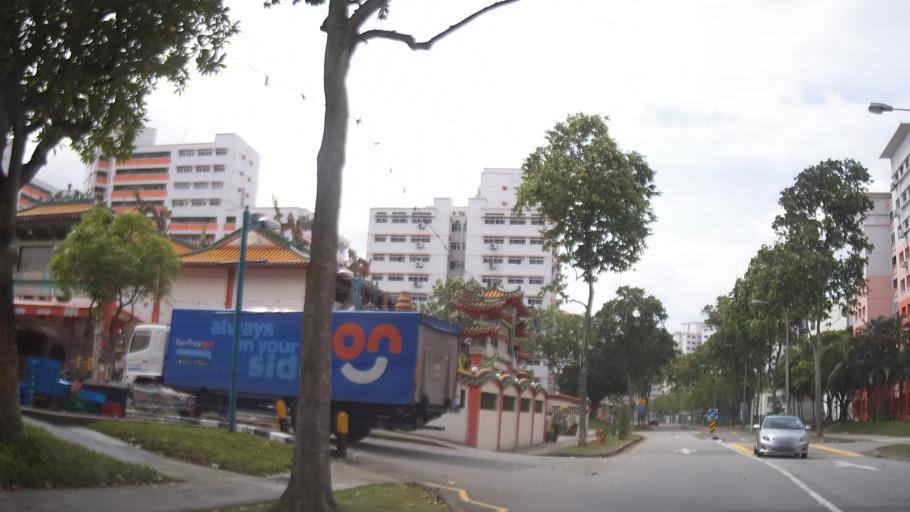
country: MY
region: Johor
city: Johor Bahru
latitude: 1.3923
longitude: 103.7426
